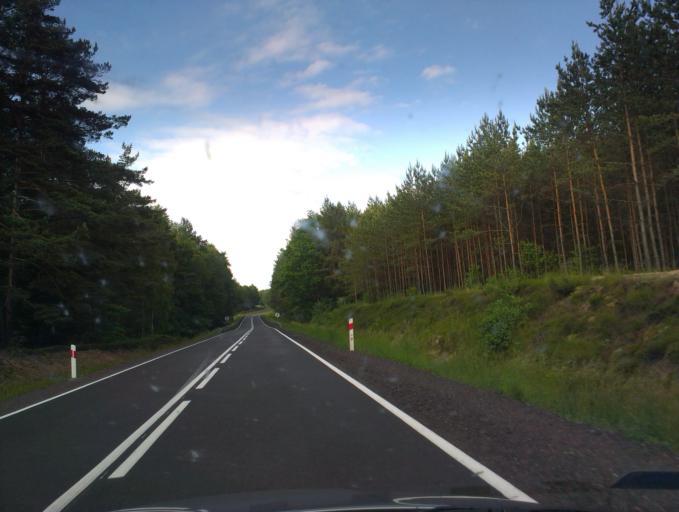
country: PL
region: West Pomeranian Voivodeship
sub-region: Powiat szczecinecki
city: Lubowo
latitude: 53.6022
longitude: 16.4385
